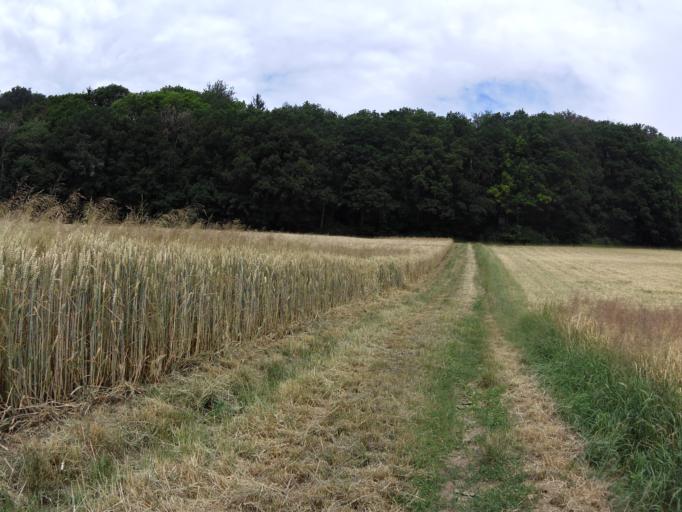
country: DE
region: Bavaria
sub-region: Regierungsbezirk Unterfranken
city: Reichenberg
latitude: 49.7149
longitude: 9.8925
